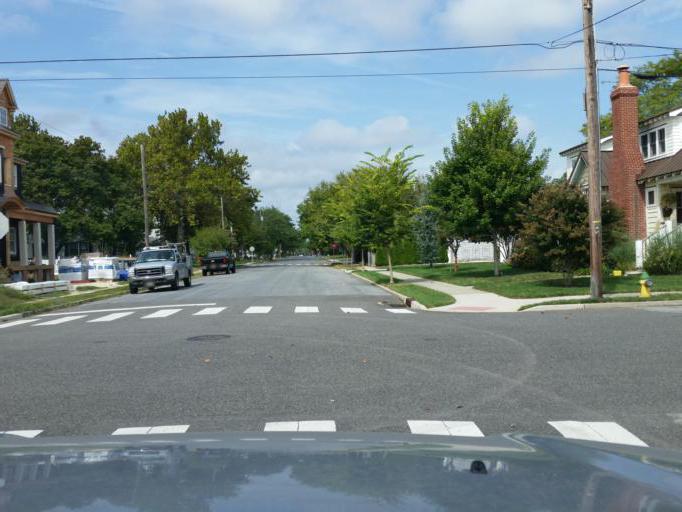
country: US
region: New Jersey
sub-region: Cape May County
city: Cape May
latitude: 38.9366
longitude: -74.9047
